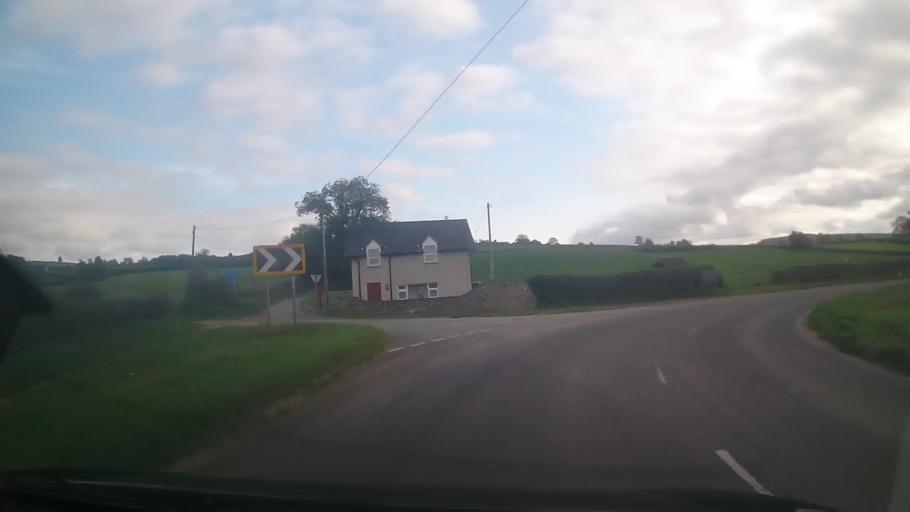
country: GB
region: England
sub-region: Shropshire
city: Bishop's Castle
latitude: 52.4837
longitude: -2.9868
